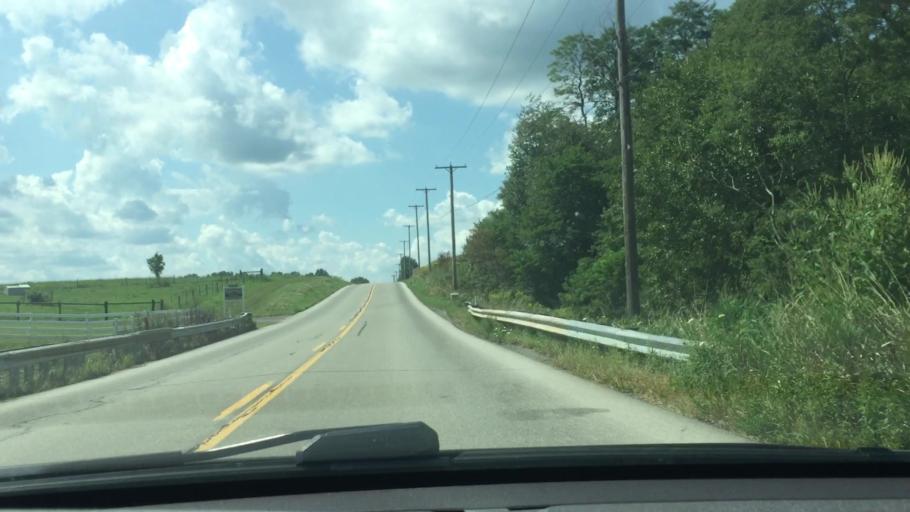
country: US
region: Pennsylvania
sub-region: Lawrence County
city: New Wilmington
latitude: 41.1204
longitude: -80.3898
